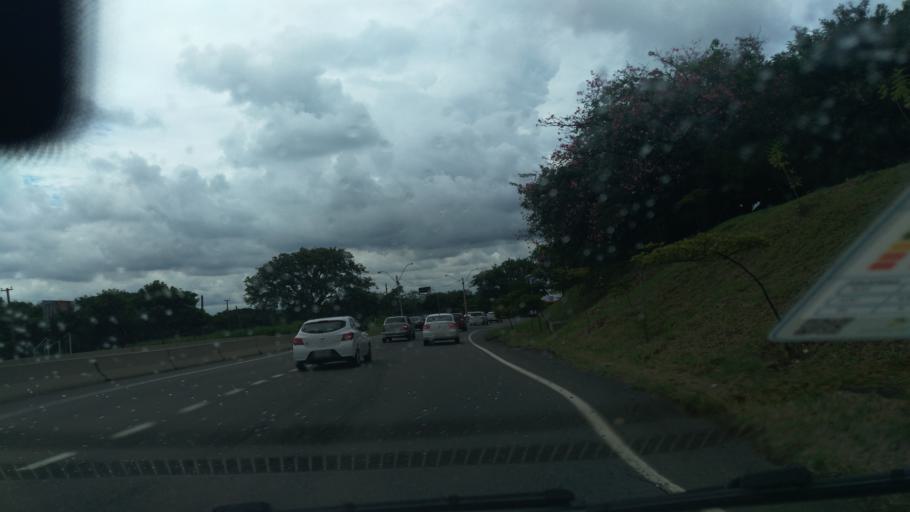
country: BR
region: Sao Paulo
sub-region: Campinas
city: Campinas
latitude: -22.8982
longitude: -47.1040
